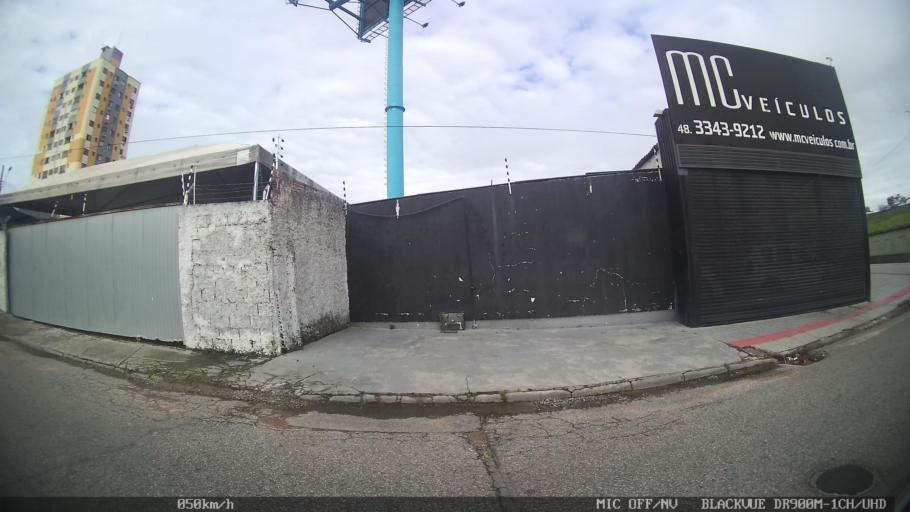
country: BR
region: Santa Catarina
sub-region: Sao Jose
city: Campinas
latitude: -27.5710
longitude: -48.6131
